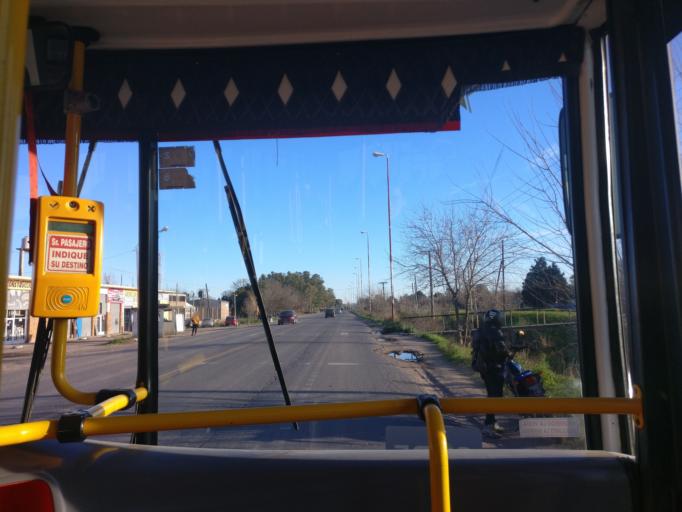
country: AR
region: Buenos Aires
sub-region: Partido de Ezeiza
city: Ezeiza
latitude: -34.9316
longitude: -58.6162
